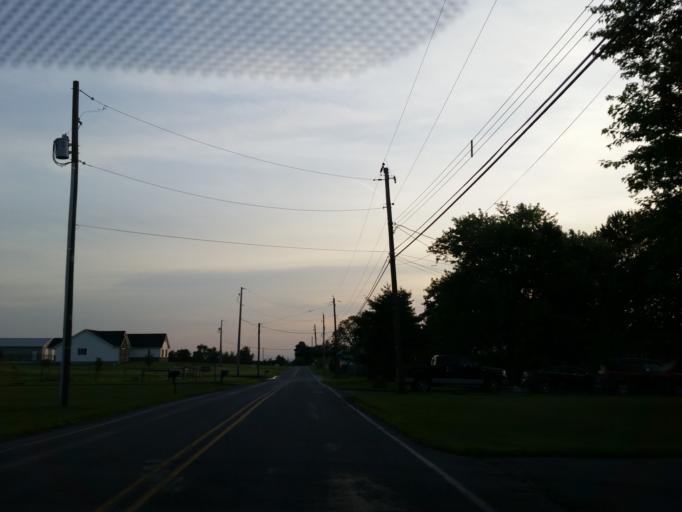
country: US
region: Pennsylvania
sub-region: Lebanon County
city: Jonestown
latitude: 40.4185
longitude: -76.5208
